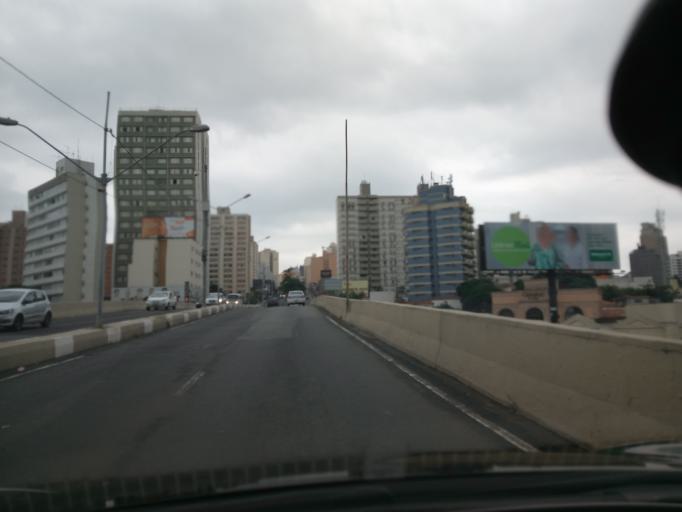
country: BR
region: Sao Paulo
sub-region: Campinas
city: Campinas
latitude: -22.9059
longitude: -47.0464
